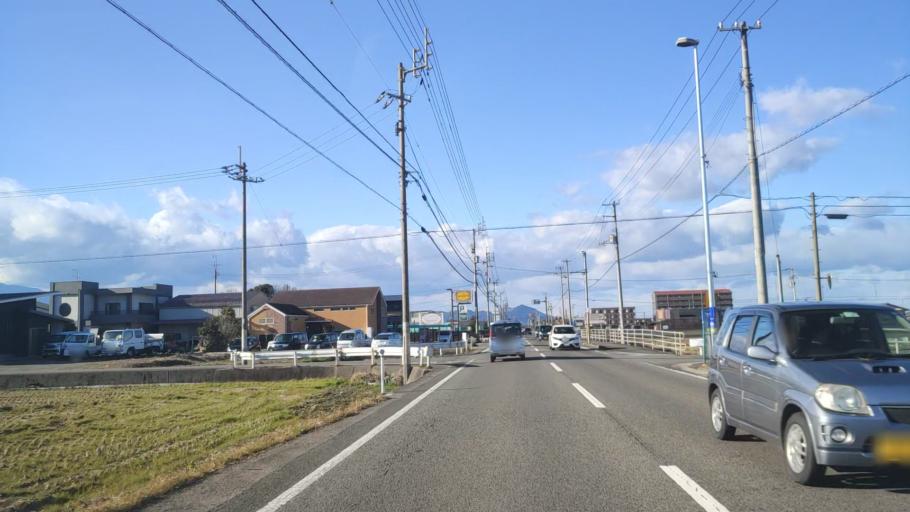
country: JP
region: Ehime
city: Saijo
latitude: 33.9118
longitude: 133.1097
